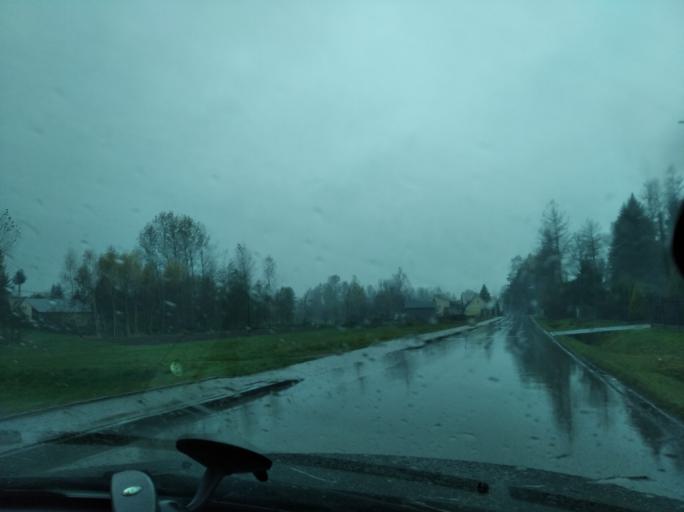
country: PL
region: Subcarpathian Voivodeship
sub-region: Powiat lancucki
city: Kraczkowa
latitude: 50.0400
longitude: 22.1793
